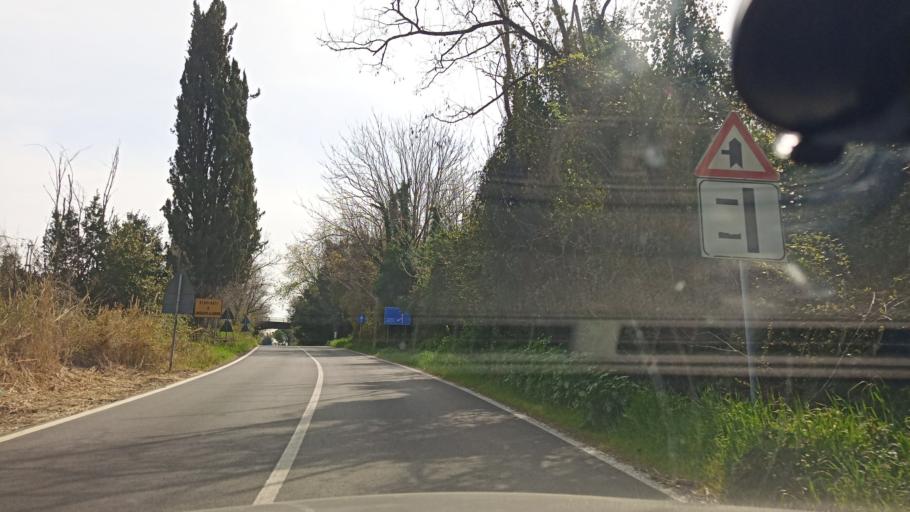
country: IT
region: Latium
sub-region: Provincia di Rieti
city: Cantalupo in Sabina
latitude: 42.3095
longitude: 12.6429
